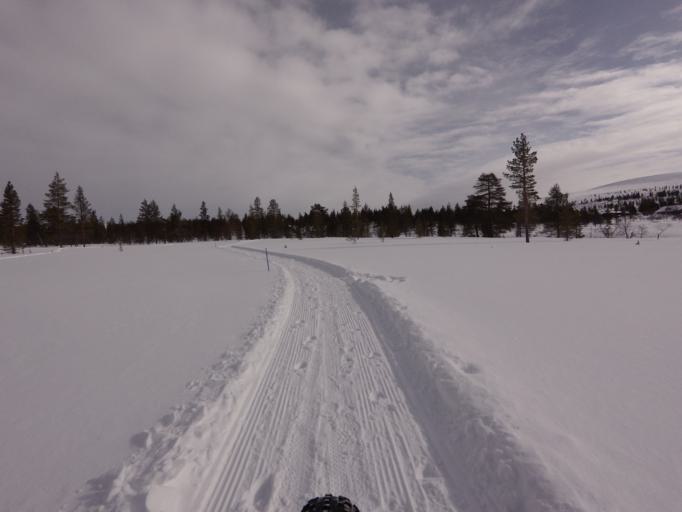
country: FI
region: Lapland
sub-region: Pohjois-Lappi
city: Ivalo
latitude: 68.3478
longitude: 27.4518
